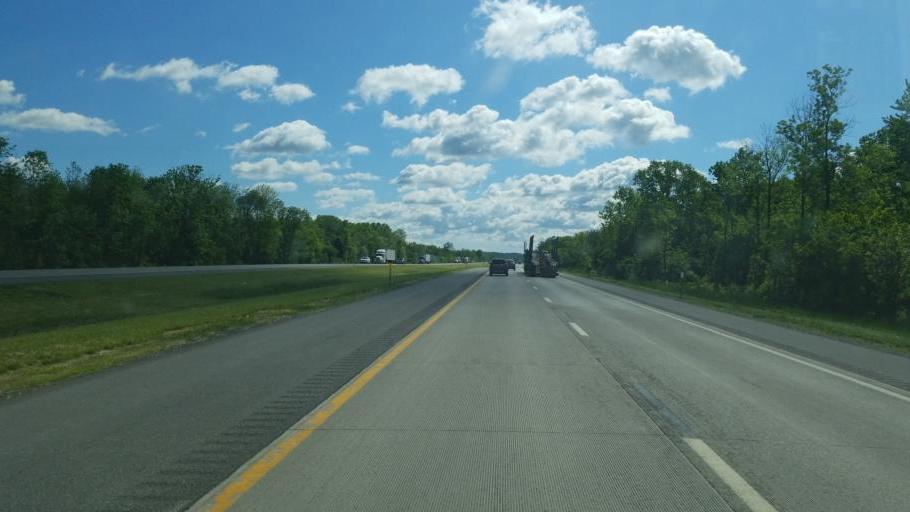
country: US
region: New York
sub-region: Onondaga County
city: Peru
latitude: 43.0865
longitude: -76.4082
